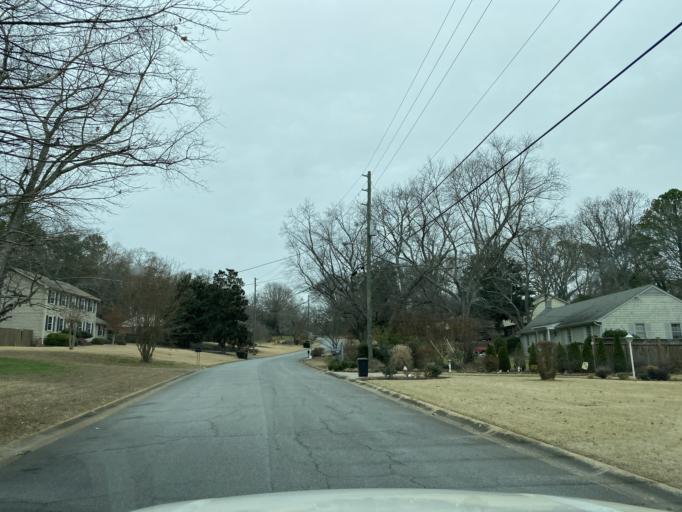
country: US
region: Georgia
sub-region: Cobb County
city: Fair Oaks
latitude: 33.9220
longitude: -84.5698
